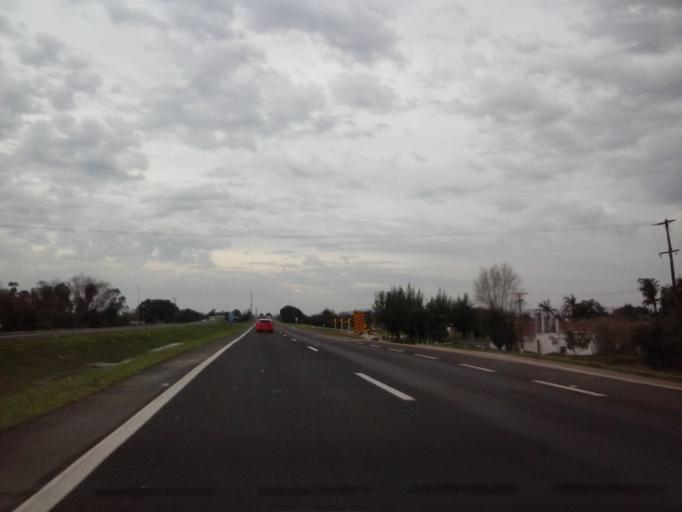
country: BR
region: Rio Grande do Sul
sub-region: Porto Alegre
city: Porto Alegre
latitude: -29.9910
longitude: -51.2292
